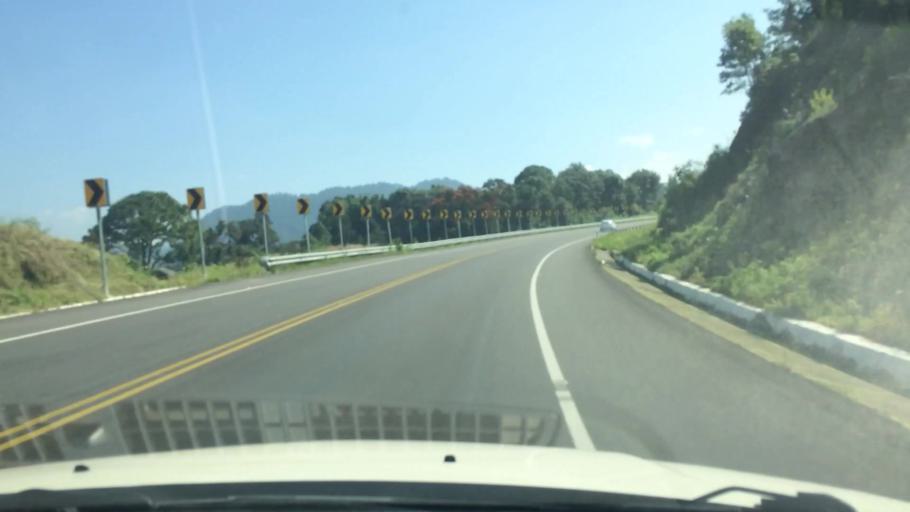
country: MX
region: Mexico
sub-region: Valle de Bravo
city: Santa Maria Pipioltepec (Pipioltepec)
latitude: 19.2192
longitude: -100.0971
